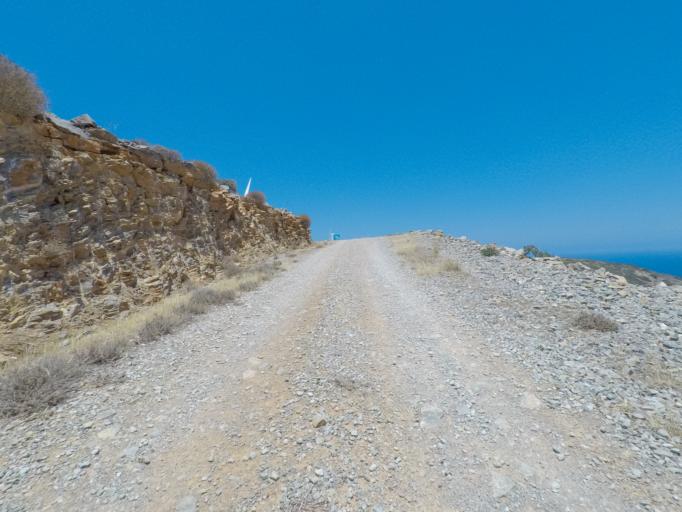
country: GR
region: Crete
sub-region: Nomos Lasithiou
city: Elounda
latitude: 35.3287
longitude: 25.7580
